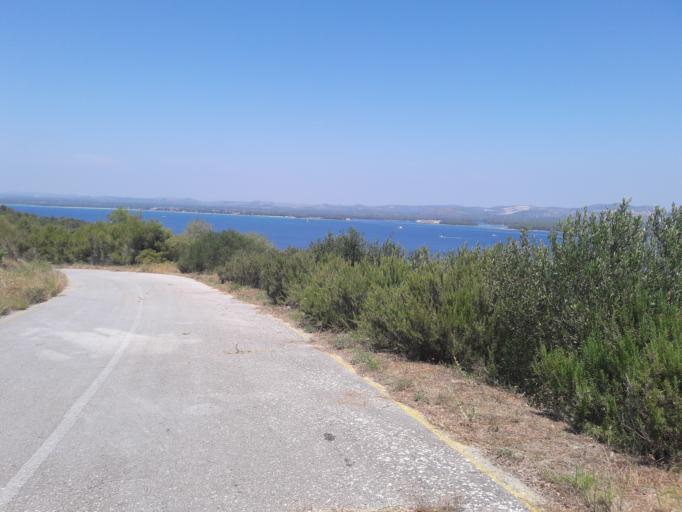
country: HR
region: Sibensko-Kniniska
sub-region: Grad Sibenik
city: Sibenik
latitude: 43.6994
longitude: 15.8479
